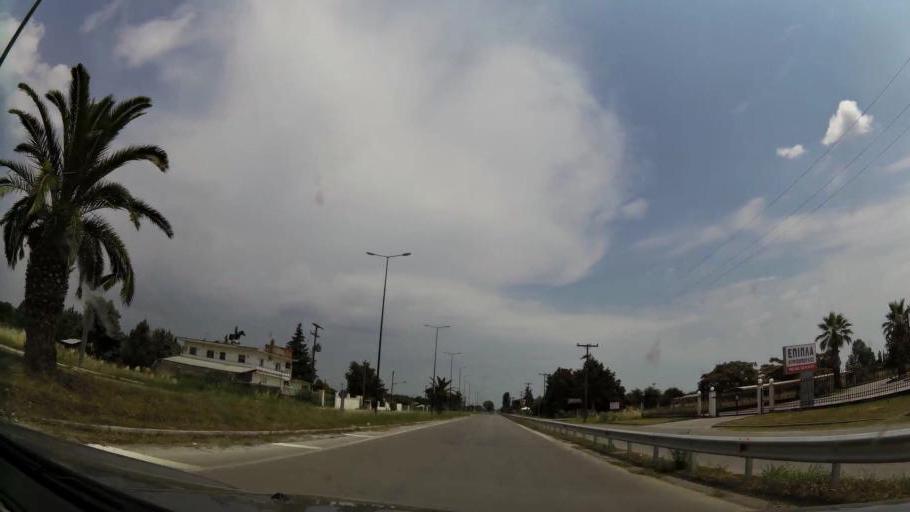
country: GR
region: Central Macedonia
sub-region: Nomos Pierias
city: Peristasi
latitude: 40.2734
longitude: 22.5476
